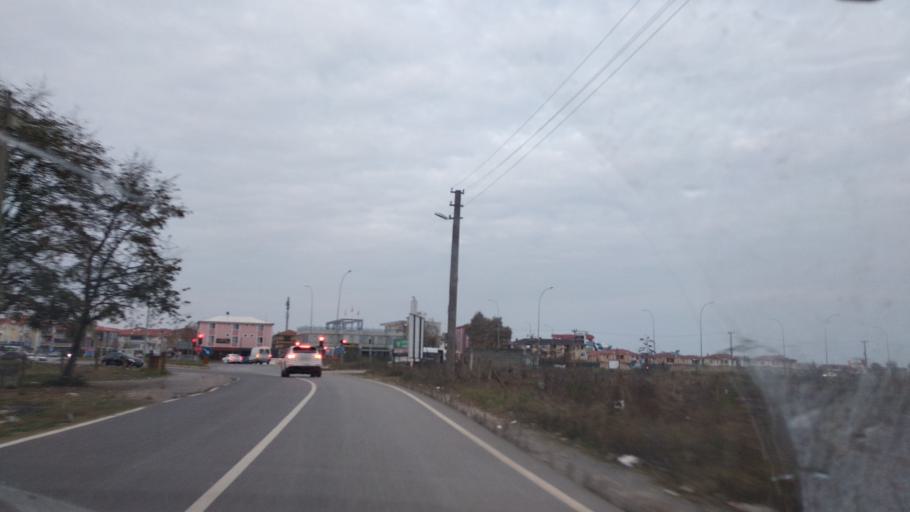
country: TR
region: Sakarya
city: Karasu
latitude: 41.0866
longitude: 30.7401
